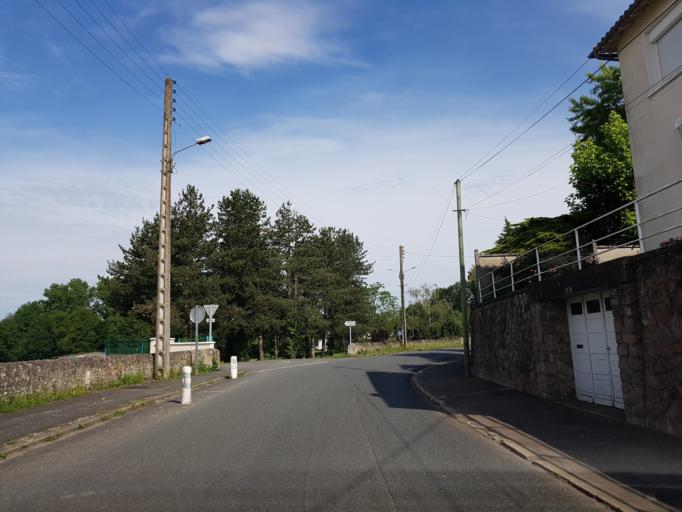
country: FR
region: Poitou-Charentes
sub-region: Departement de la Charente
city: Chabanais
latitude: 45.8779
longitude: 0.7155
